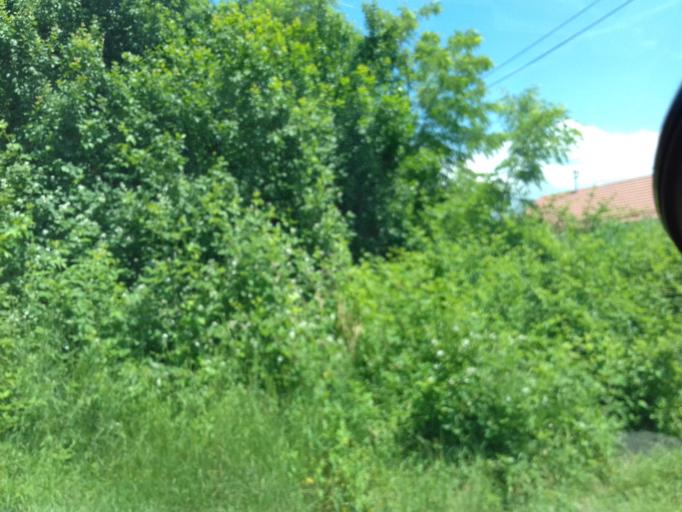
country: BA
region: Federation of Bosnia and Herzegovina
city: Kobilja Glava
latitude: 43.8674
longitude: 18.4252
